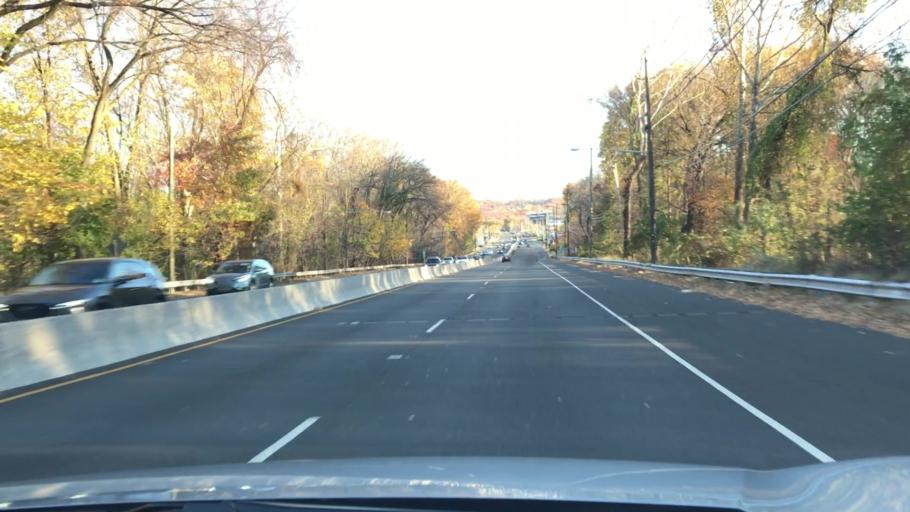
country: US
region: New Jersey
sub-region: Bergen County
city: Englewood
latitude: 40.8860
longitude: -73.9926
